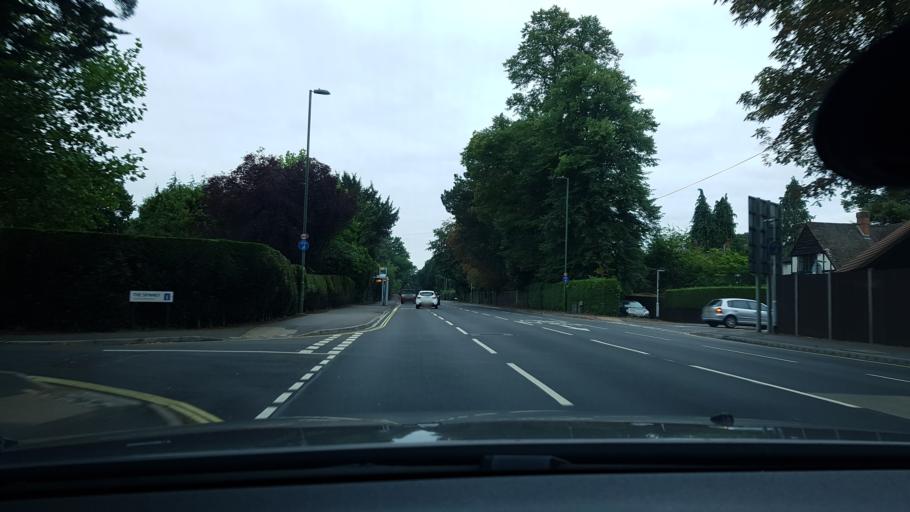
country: GB
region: England
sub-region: Southampton
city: Southampton
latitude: 50.9507
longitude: -1.4043
